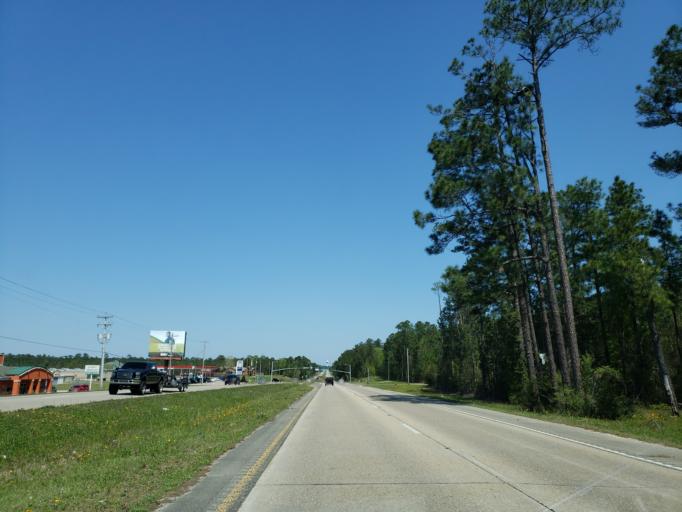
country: US
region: Mississippi
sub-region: Harrison County
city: Lyman
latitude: 30.5528
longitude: -89.1208
